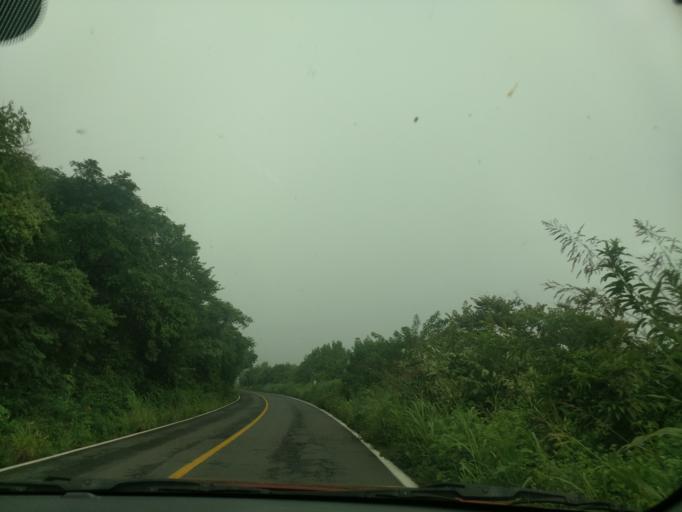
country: MX
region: Jalisco
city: Ameca
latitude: 20.5444
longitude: -104.1472
